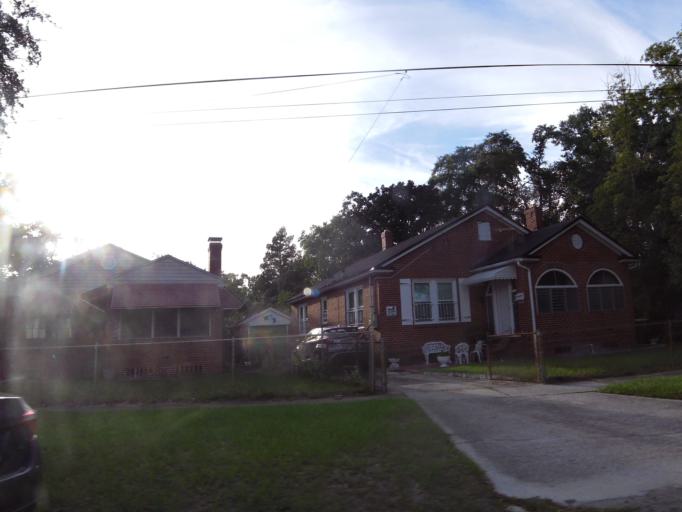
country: US
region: Florida
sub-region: Duval County
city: Jacksonville
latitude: 30.3791
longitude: -81.6568
